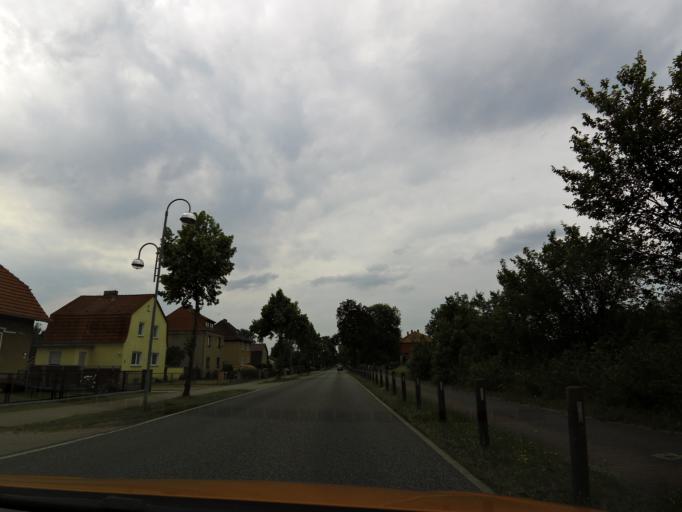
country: DE
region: Brandenburg
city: Zossen
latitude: 52.1994
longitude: 13.4580
